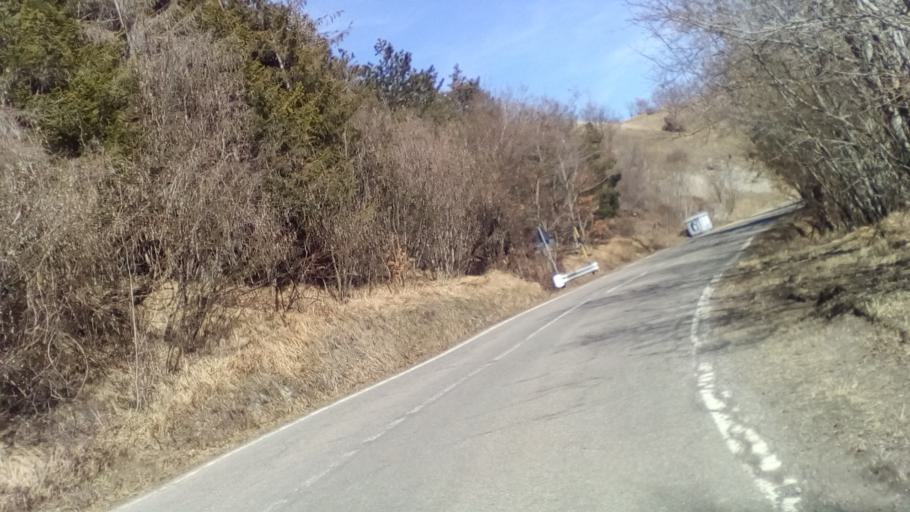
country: IT
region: Emilia-Romagna
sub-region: Provincia di Modena
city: Pievepelago
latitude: 44.2255
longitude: 10.6266
